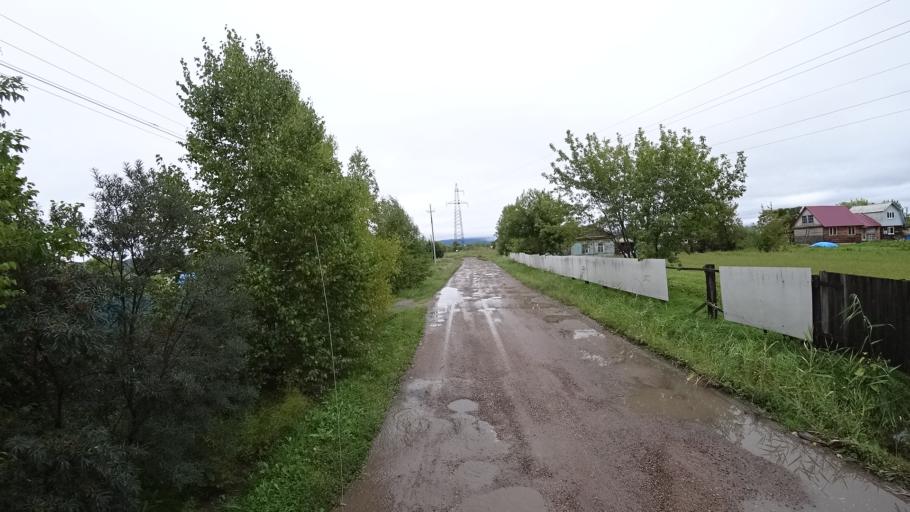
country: RU
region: Primorskiy
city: Monastyrishche
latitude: 44.2006
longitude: 132.4749
